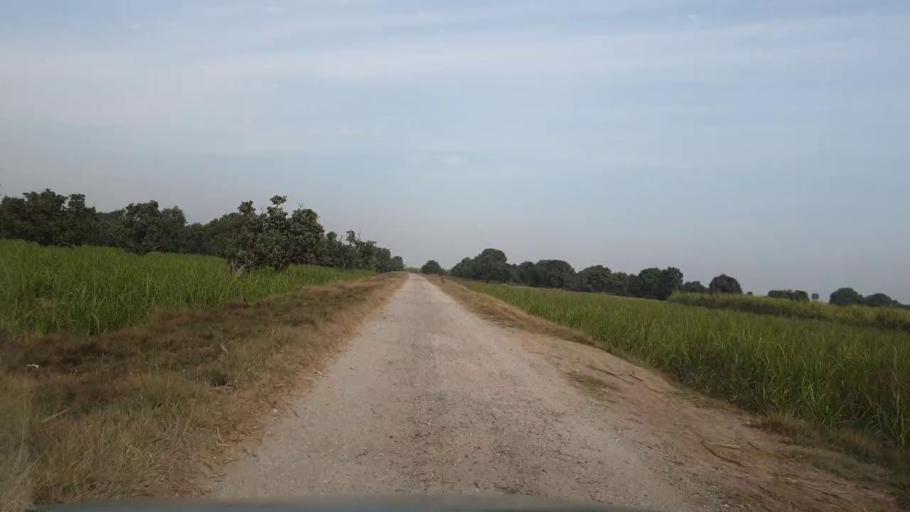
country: PK
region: Sindh
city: Matiari
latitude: 25.5604
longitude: 68.5410
